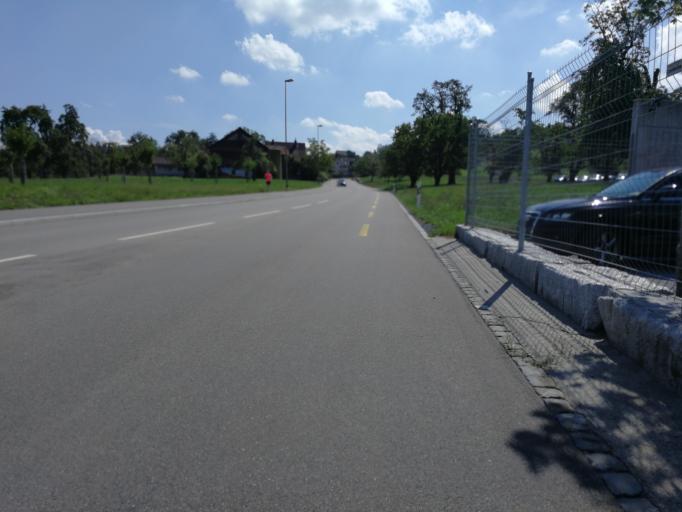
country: CH
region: Zurich
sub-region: Bezirk Horgen
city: Horgen / Allmend
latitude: 47.2505
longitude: 8.6183
